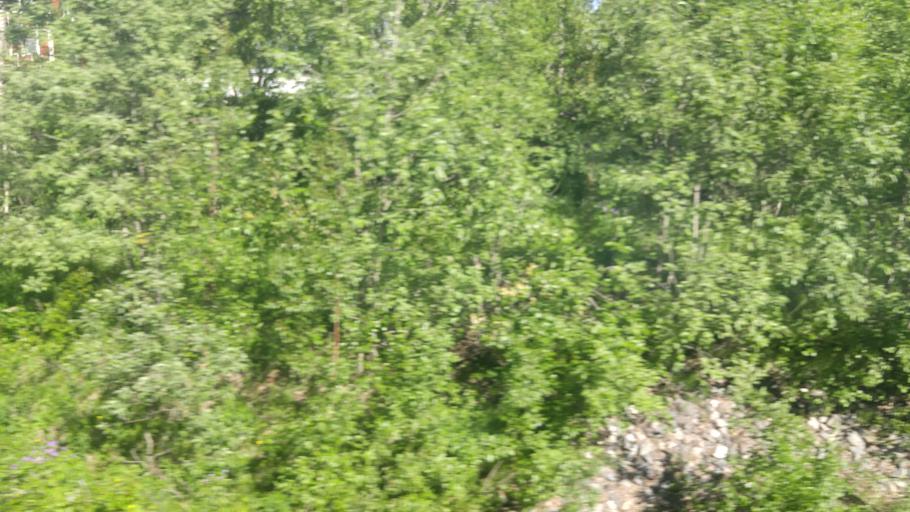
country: SE
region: Jaemtland
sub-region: Are Kommun
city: Are
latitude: 63.3201
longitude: 12.5341
